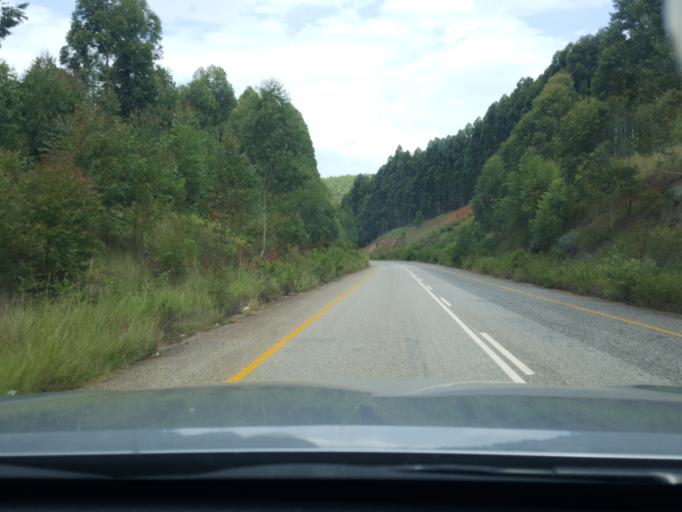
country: ZA
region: Mpumalanga
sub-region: Ehlanzeni District
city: White River
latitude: -25.1846
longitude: 30.8888
